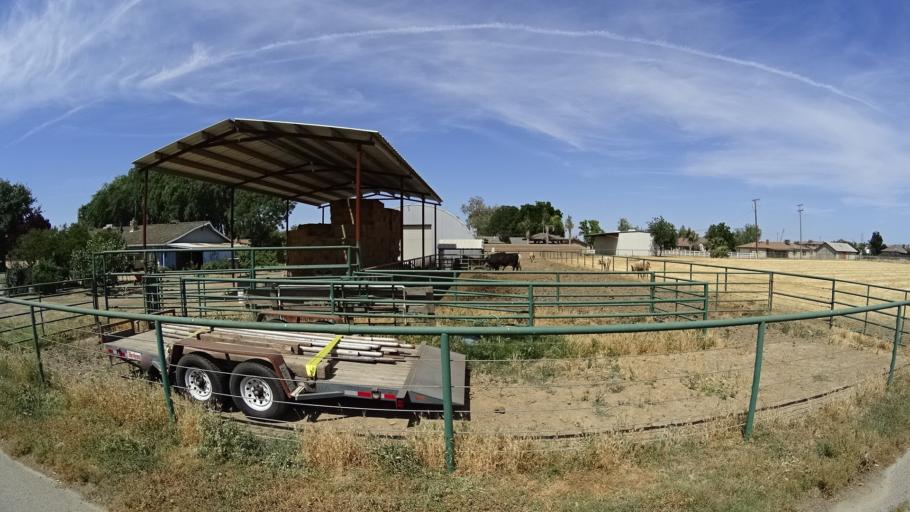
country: US
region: California
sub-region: Kings County
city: Home Garden
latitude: 36.3297
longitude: -119.5884
